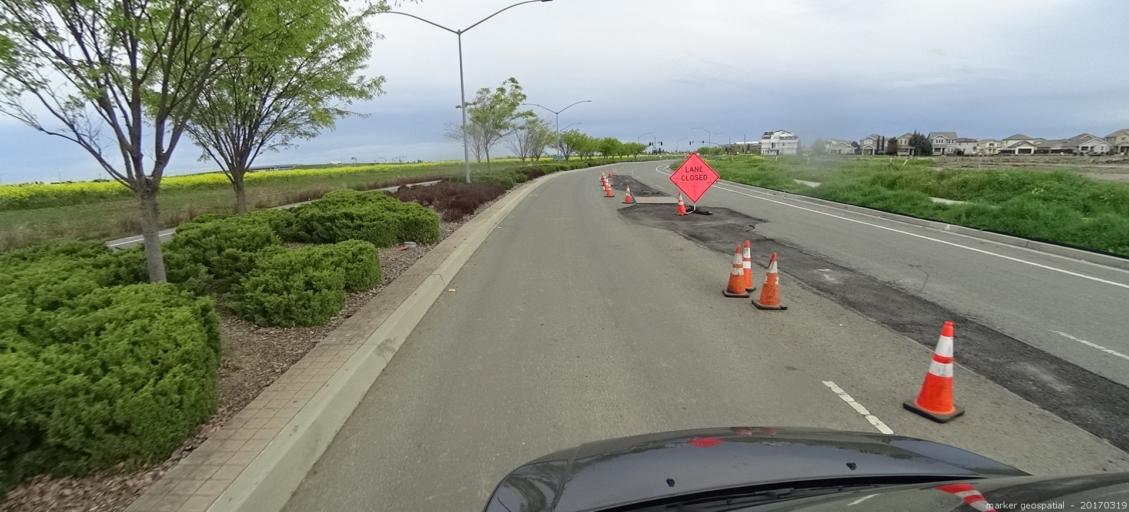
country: US
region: California
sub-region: Yolo County
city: West Sacramento
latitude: 38.6374
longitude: -121.5199
